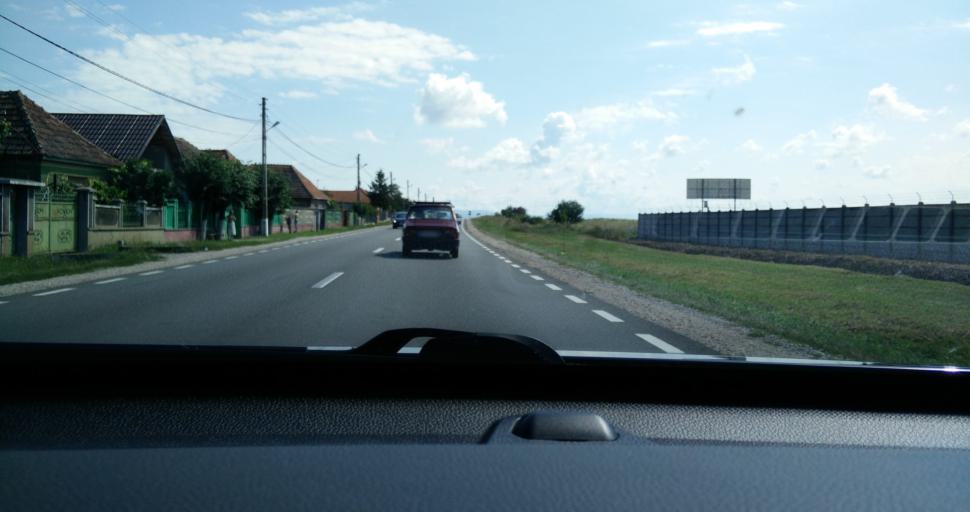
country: RO
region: Bihor
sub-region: Comuna Sacadat
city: Sacadat
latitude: 47.0619
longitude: 22.1524
